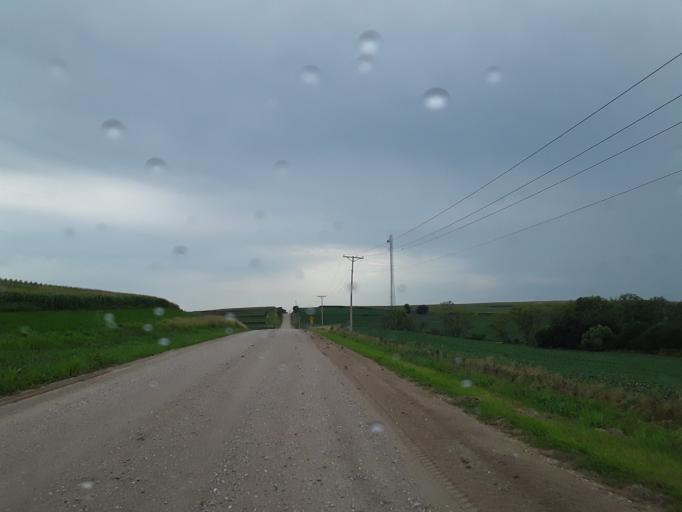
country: US
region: Nebraska
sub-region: Washington County
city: Blair
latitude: 41.5092
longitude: -96.1695
